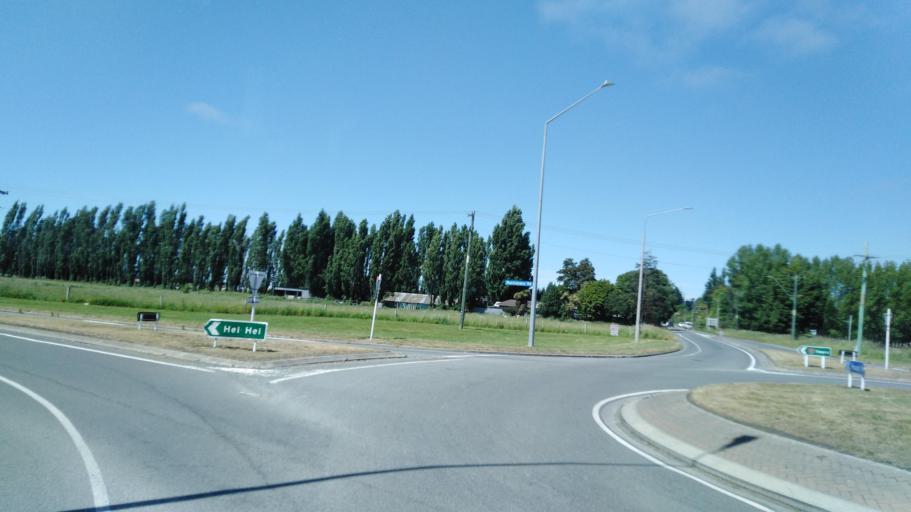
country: NZ
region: Canterbury
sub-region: Selwyn District
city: Prebbleton
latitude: -43.5194
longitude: 172.5051
